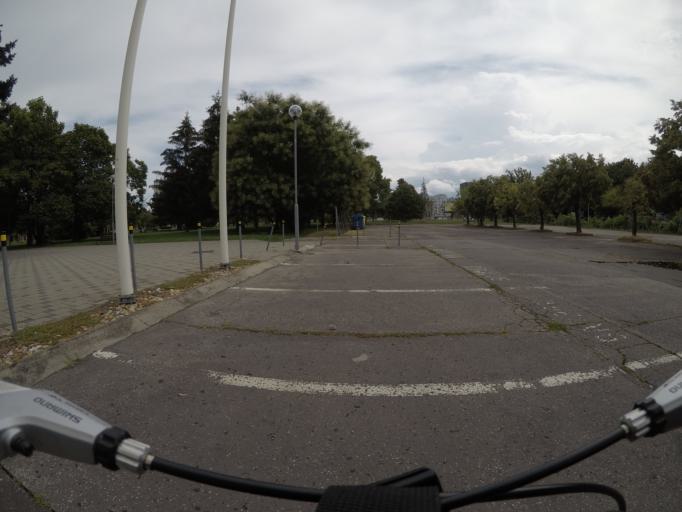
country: SK
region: Bratislavsky
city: Bratislava
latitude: 48.1590
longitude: 17.1631
